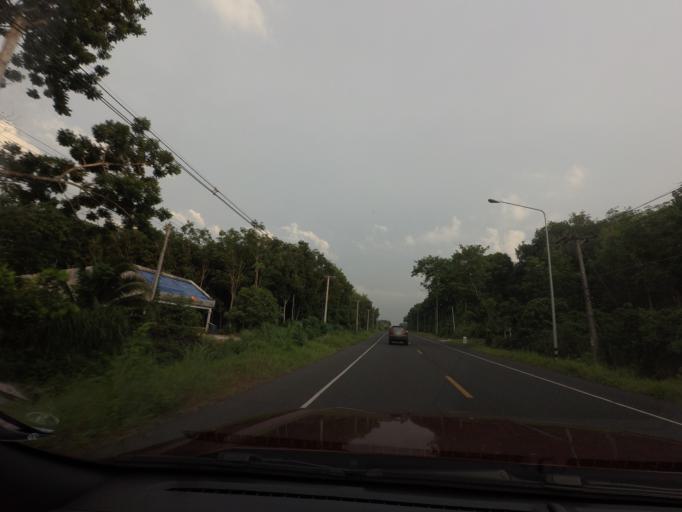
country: TH
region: Pattani
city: Mae Lan
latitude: 6.6082
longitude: 101.1920
